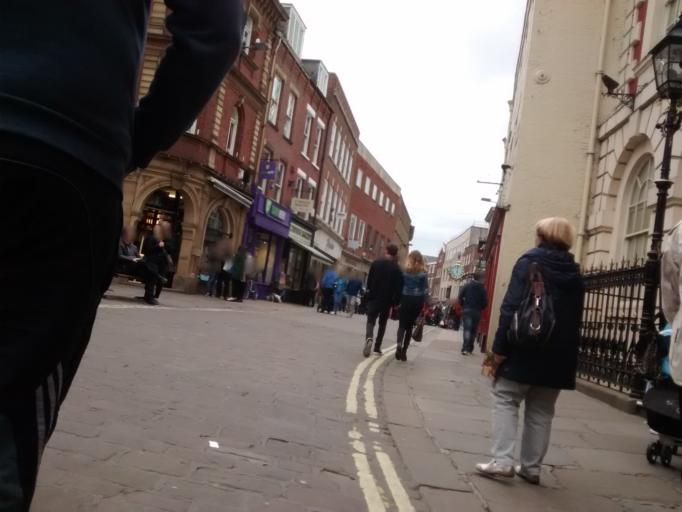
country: GB
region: England
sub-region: City of York
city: York
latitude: 53.9600
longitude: -1.0849
